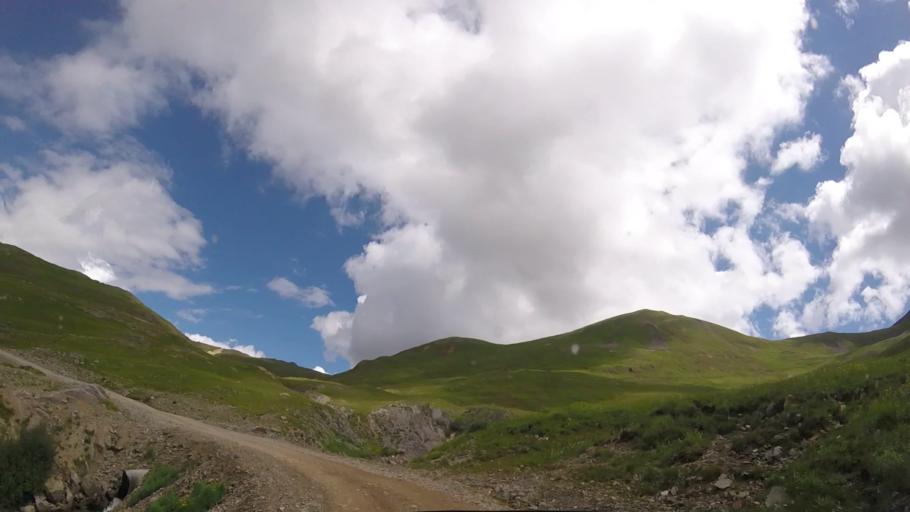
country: US
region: Colorado
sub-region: Ouray County
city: Ouray
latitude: 37.9502
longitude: -107.5728
